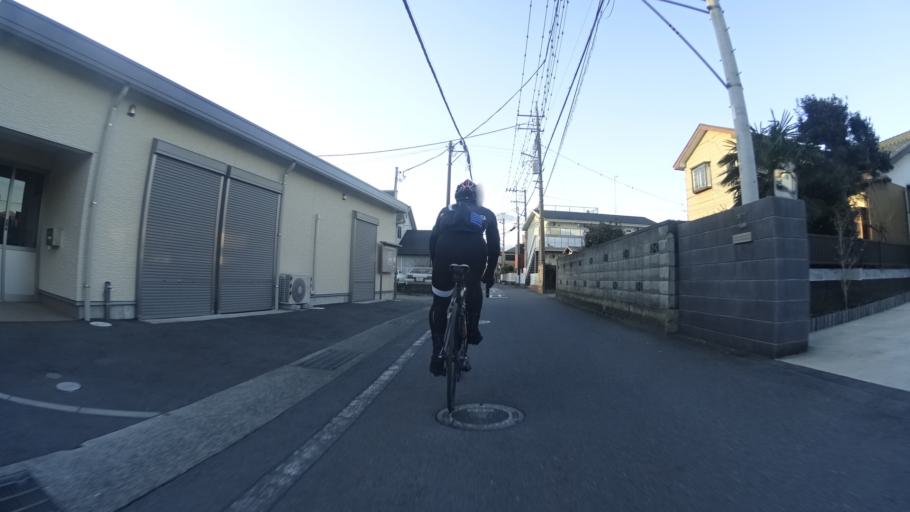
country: JP
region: Kanagawa
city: Atsugi
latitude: 35.4626
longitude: 139.3687
